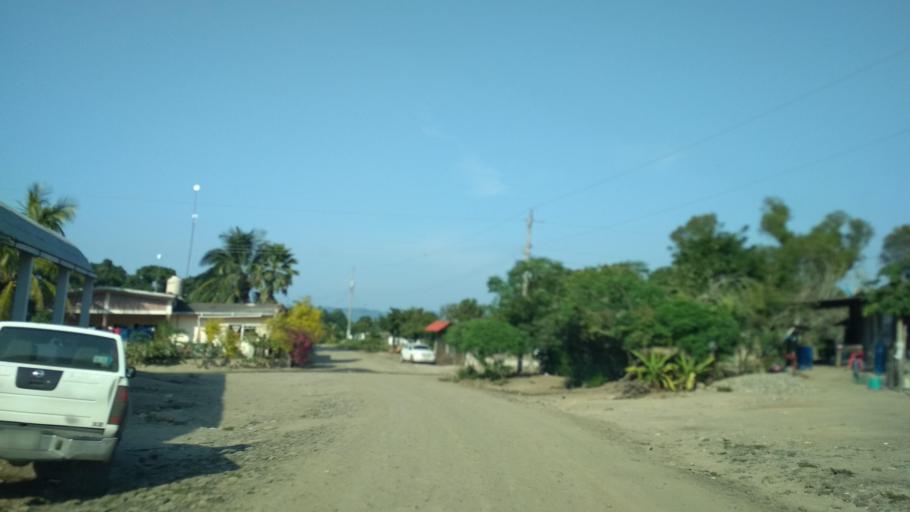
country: MX
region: Puebla
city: San Jose Acateno
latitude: 20.2166
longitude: -97.2640
